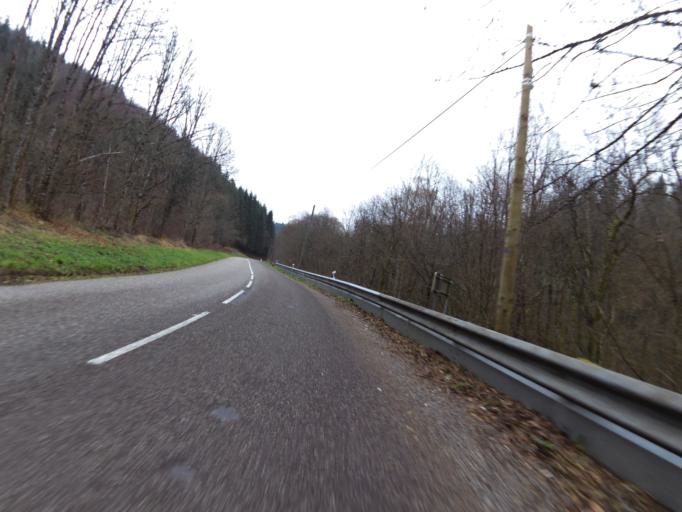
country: FR
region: Alsace
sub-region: Departement du Haut-Rhin
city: Ferrette
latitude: 47.4390
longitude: 7.3205
